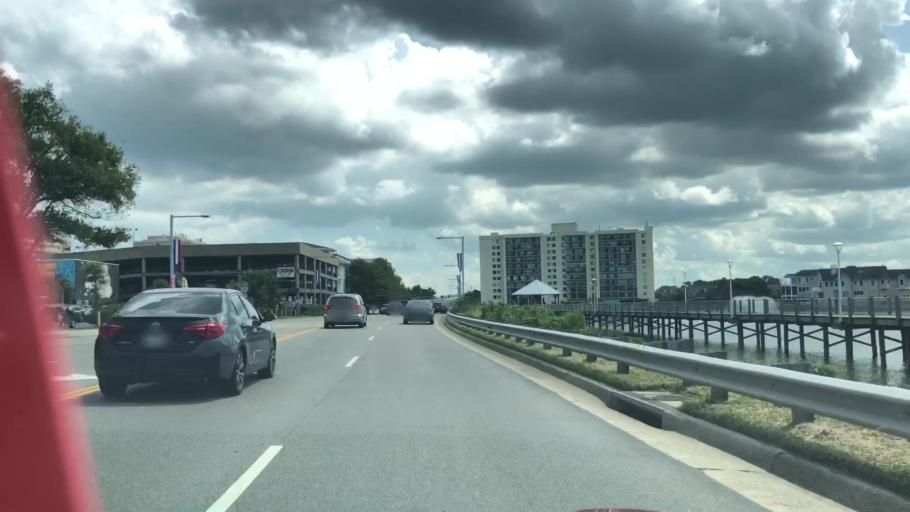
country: US
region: Virginia
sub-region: City of Virginia Beach
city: Virginia Beach
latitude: 36.8370
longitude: -75.9734
